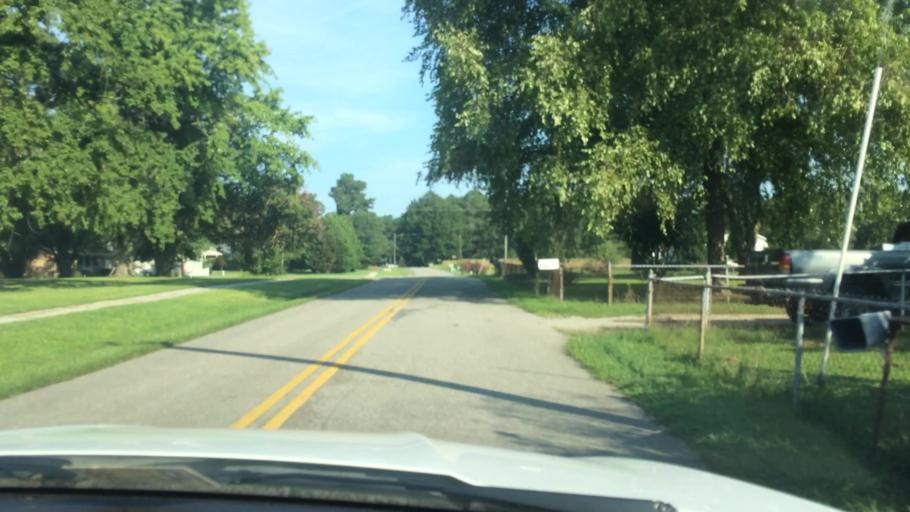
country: US
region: Virginia
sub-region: King William County
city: West Point
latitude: 37.5624
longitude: -76.7969
